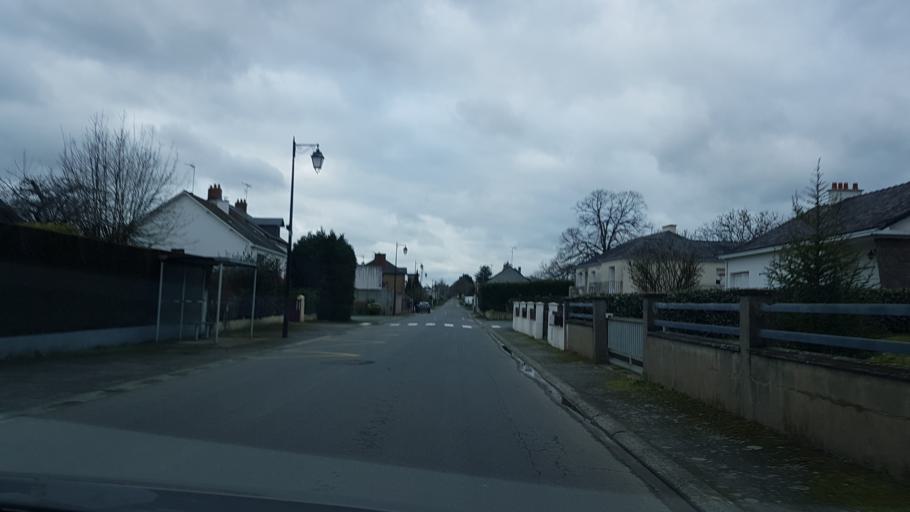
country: FR
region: Pays de la Loire
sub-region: Departement de la Loire-Atlantique
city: Le Gavre
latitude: 47.5214
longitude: -1.7505
